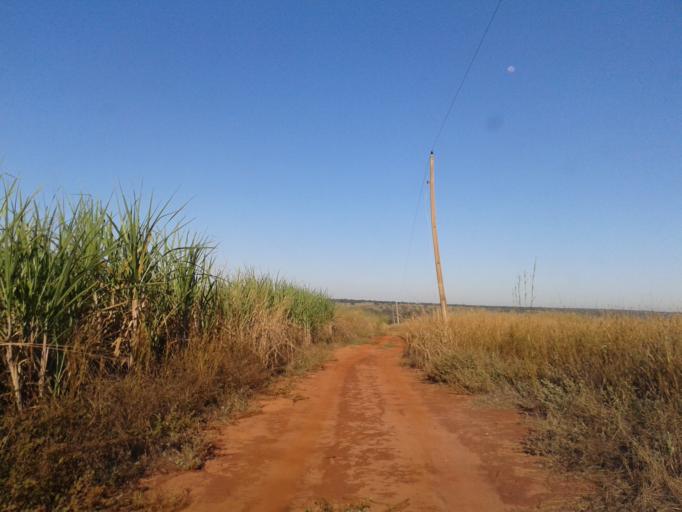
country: BR
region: Minas Gerais
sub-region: Santa Vitoria
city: Santa Vitoria
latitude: -19.0214
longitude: -50.3624
